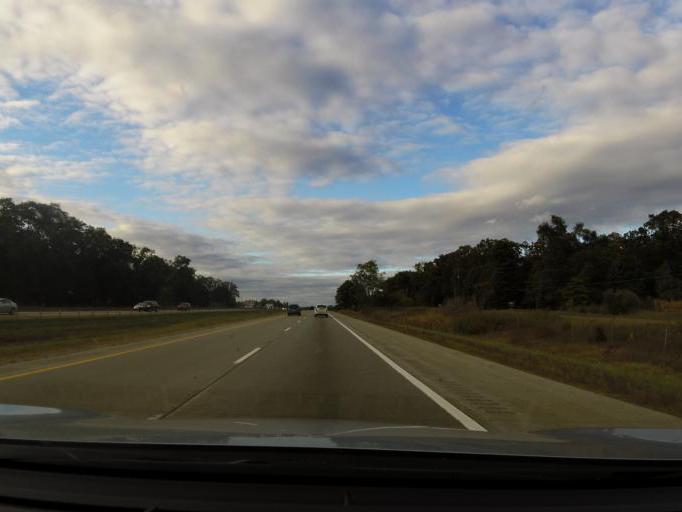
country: US
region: Michigan
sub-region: Genesee County
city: Fenton
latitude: 42.7179
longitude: -83.7626
